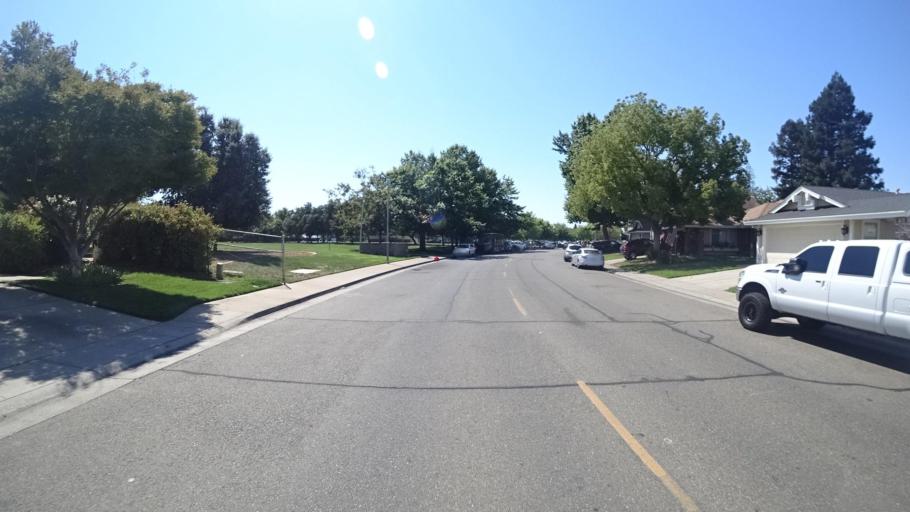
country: US
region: California
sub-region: Sacramento County
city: Laguna
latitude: 38.4174
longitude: -121.4107
